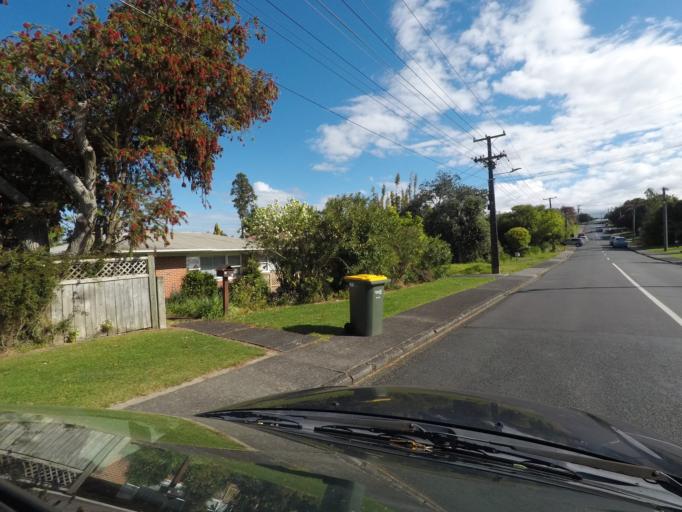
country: NZ
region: Auckland
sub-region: Auckland
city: Rosebank
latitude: -36.8668
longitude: 174.6514
